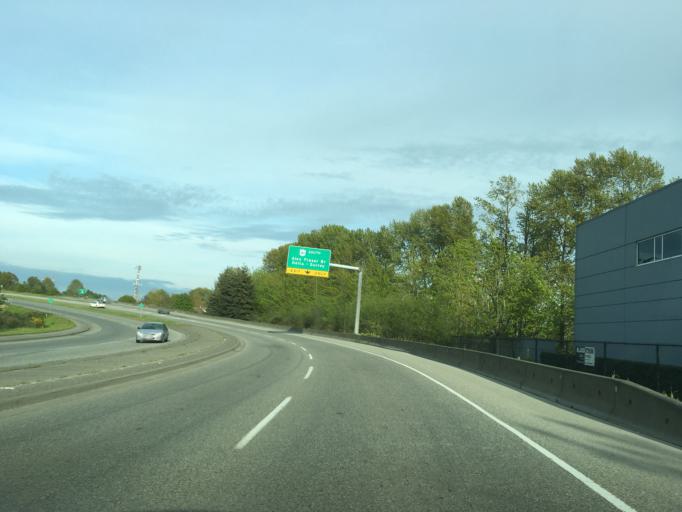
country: CA
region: British Columbia
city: Delta
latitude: 49.1680
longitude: -122.9751
